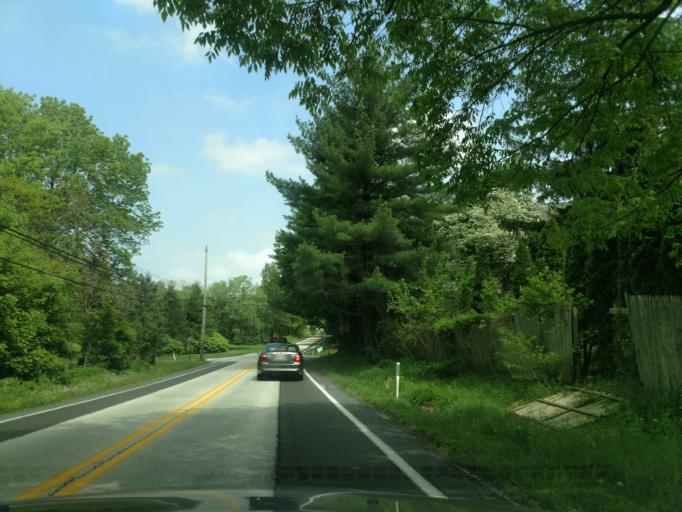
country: US
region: Pennsylvania
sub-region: Chester County
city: Kenilworth
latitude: 40.1765
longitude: -75.6392
